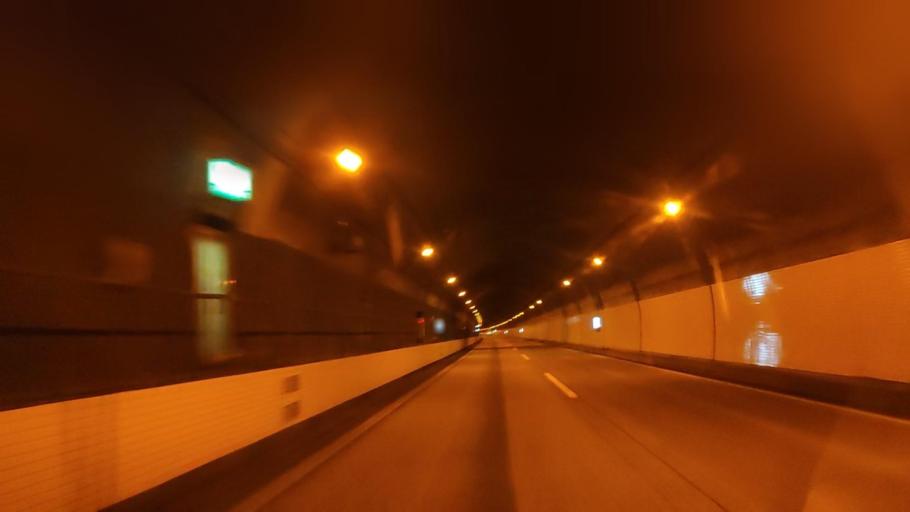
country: JP
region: Toyama
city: Nyuzen
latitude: 36.9767
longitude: 137.6552
